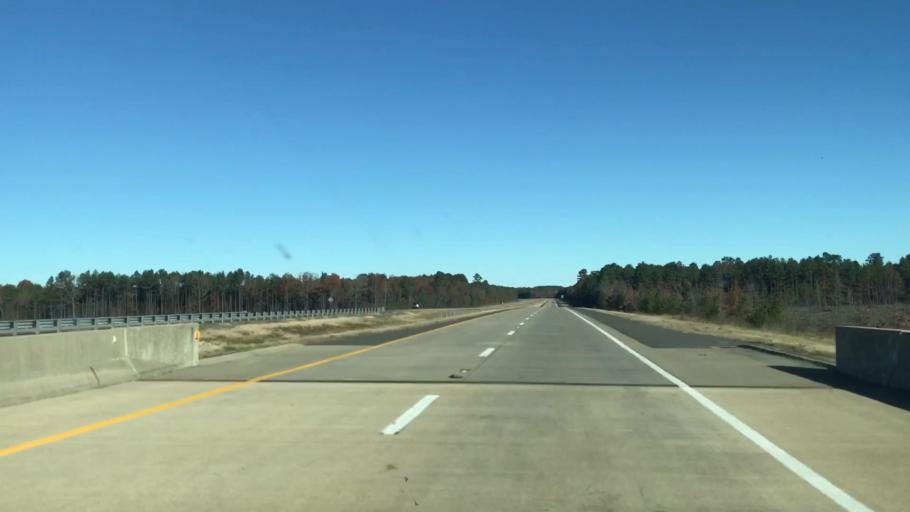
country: US
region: Texas
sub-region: Bowie County
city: Texarkana
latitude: 33.2250
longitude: -93.8732
